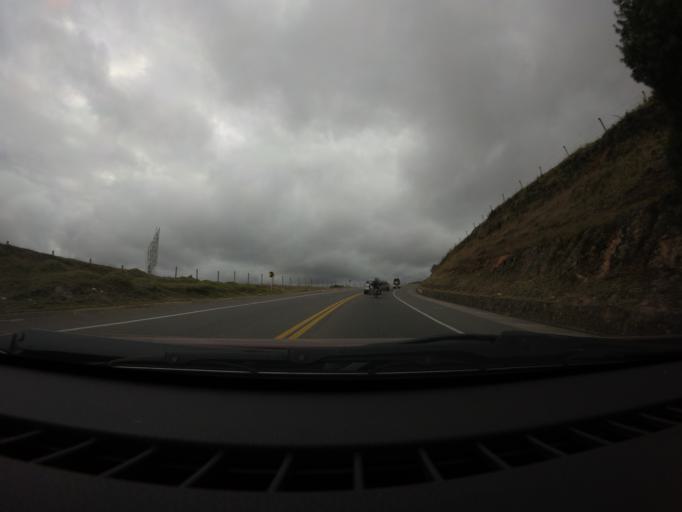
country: CO
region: Boyaca
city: Tunja
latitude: 5.4880
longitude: -73.3856
